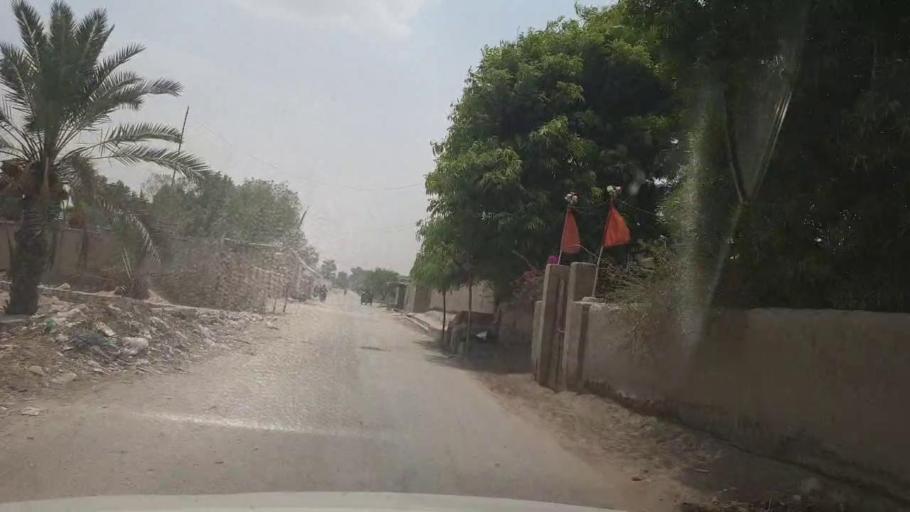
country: PK
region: Sindh
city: Kot Diji
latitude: 27.3701
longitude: 68.7221
